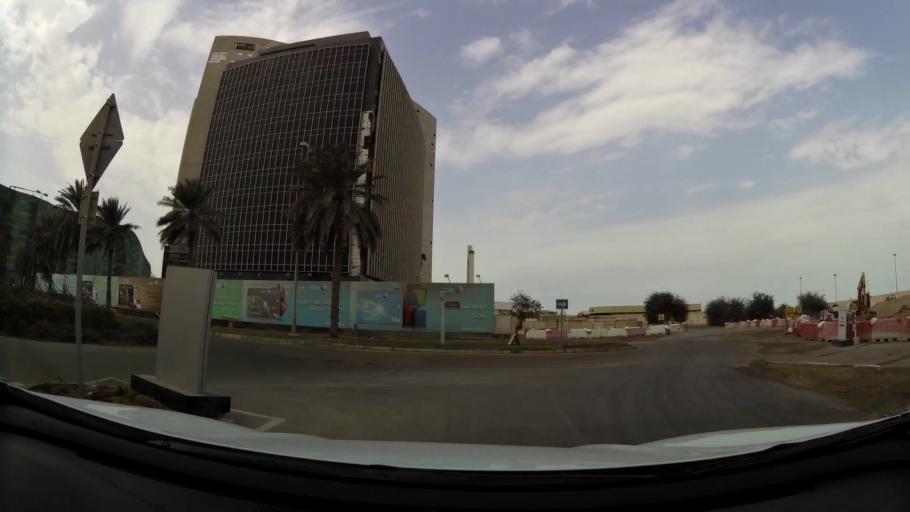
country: AE
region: Abu Dhabi
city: Abu Dhabi
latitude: 24.4224
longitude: 54.4591
